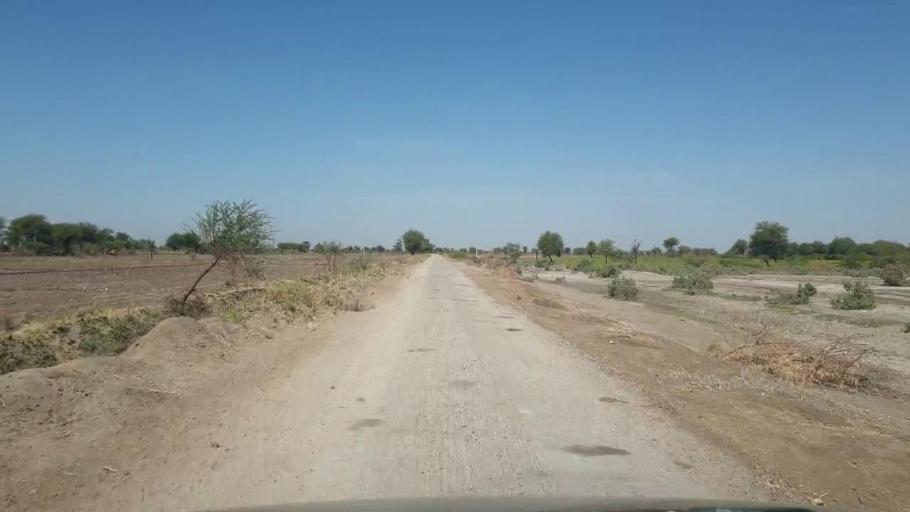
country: PK
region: Sindh
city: Dhoro Naro
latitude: 25.4319
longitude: 69.6195
